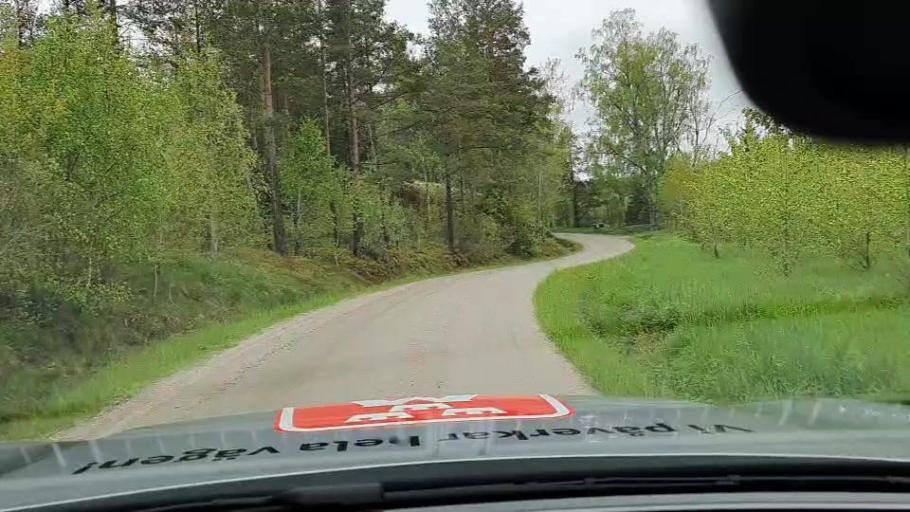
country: SE
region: Soedermanland
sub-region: Nykopings Kommun
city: Svalsta
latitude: 58.6257
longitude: 16.9404
